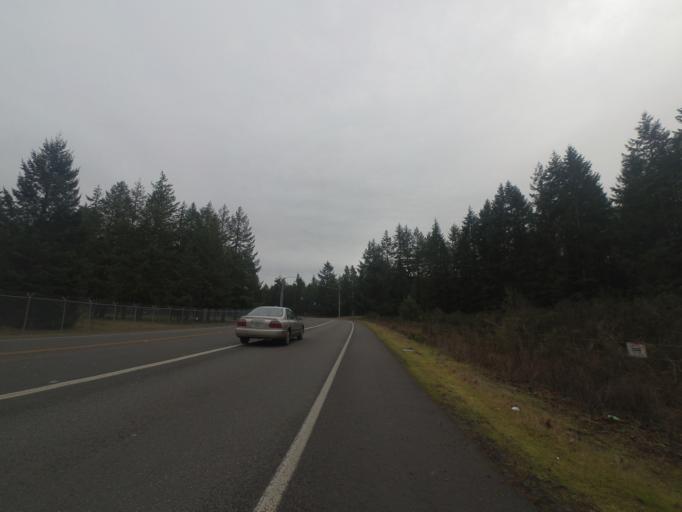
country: US
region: Washington
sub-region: Pierce County
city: McChord Air Force Base
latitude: 47.1149
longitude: -122.4956
